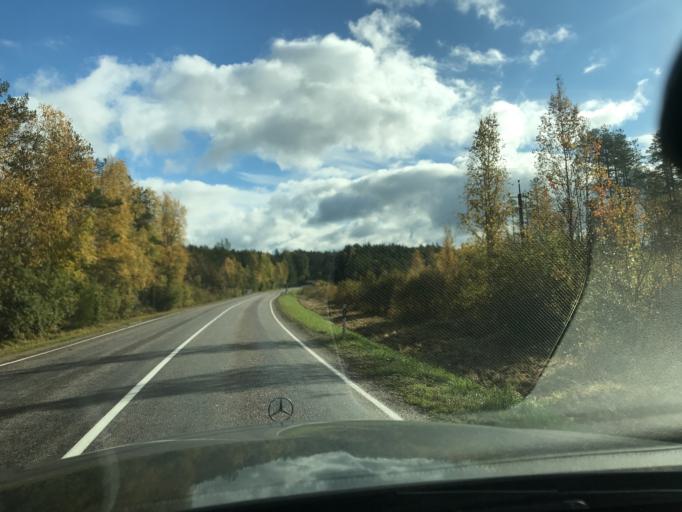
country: EE
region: Valgamaa
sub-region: Torva linn
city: Torva
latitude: 58.0102
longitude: 26.1358
